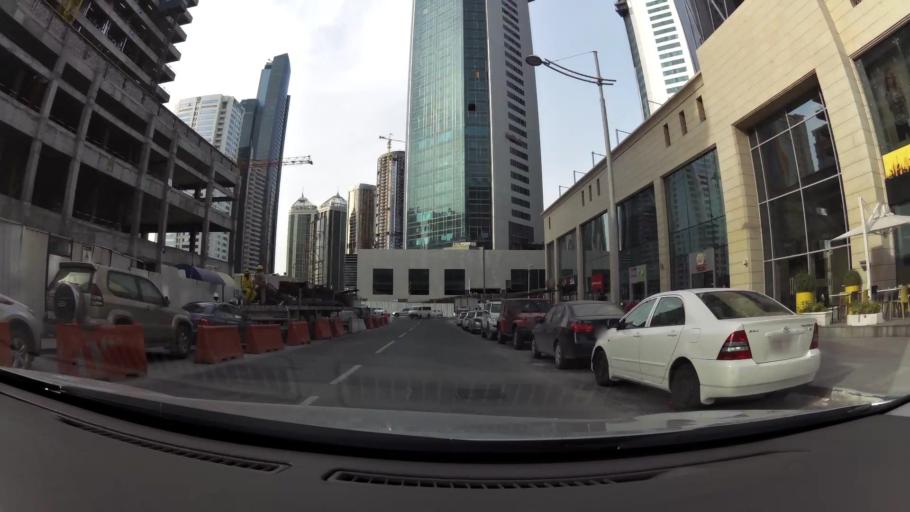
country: QA
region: Baladiyat ad Dawhah
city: Doha
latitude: 25.3232
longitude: 51.5260
